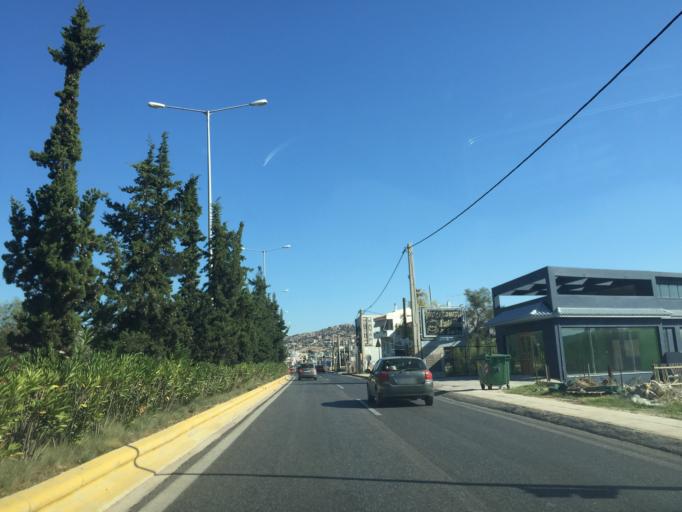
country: GR
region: Attica
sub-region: Nomarchia Anatolikis Attikis
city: Vari
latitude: 37.8420
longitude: 23.8170
